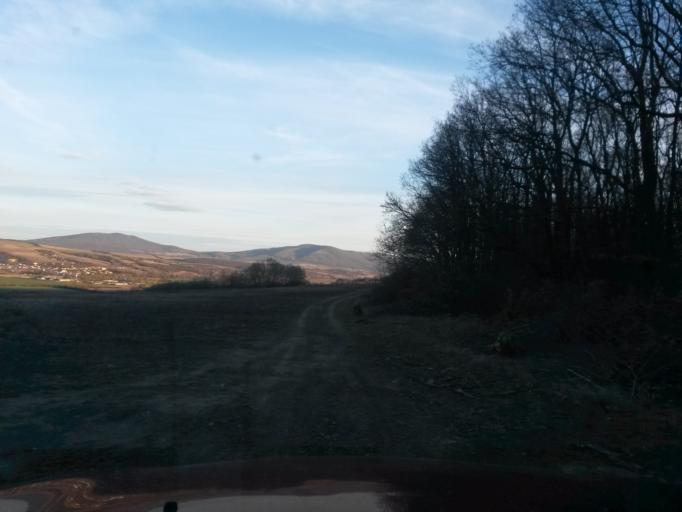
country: SK
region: Kosicky
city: Kosice
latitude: 48.7043
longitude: 21.3055
